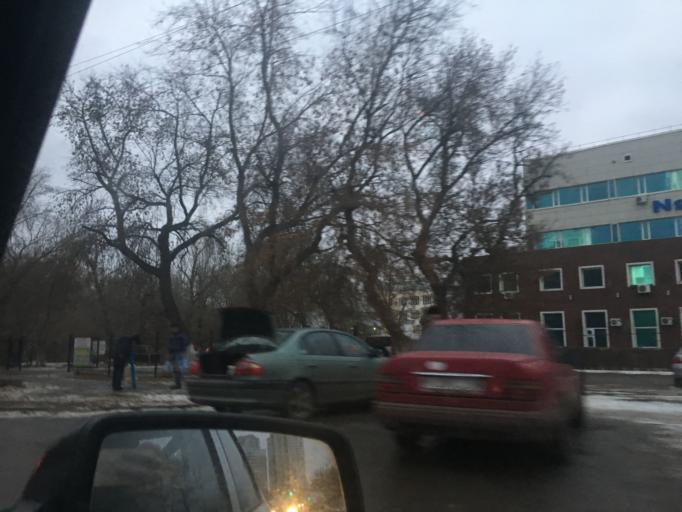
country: KZ
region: Astana Qalasy
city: Astana
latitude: 51.1664
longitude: 71.4477
